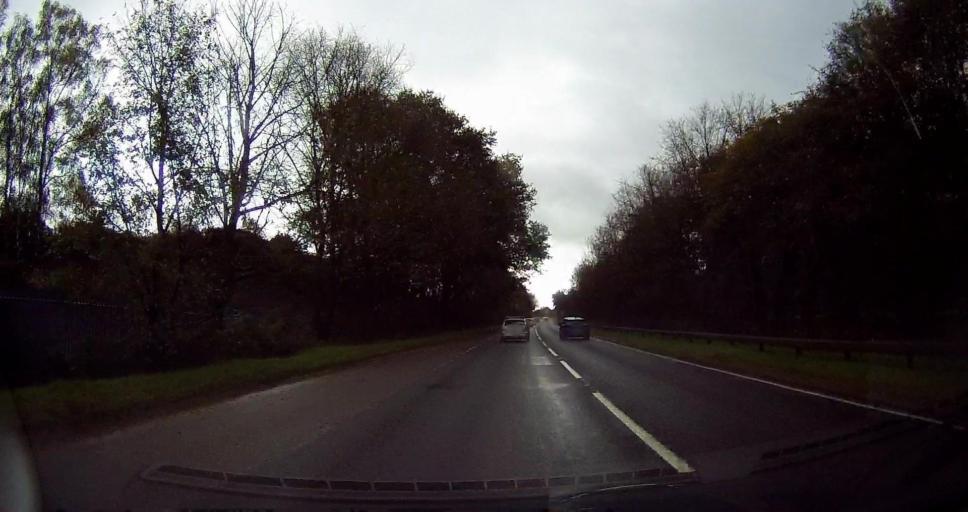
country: GB
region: England
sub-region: Staffordshire
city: Shenstone
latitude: 52.6194
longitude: -1.7980
